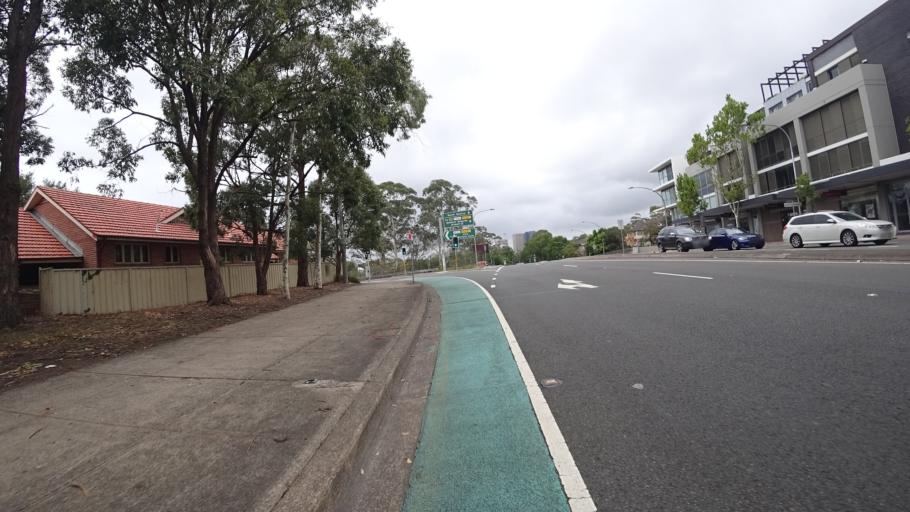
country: AU
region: New South Wales
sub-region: North Sydney
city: Cammeray
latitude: -33.8232
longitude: 151.2103
